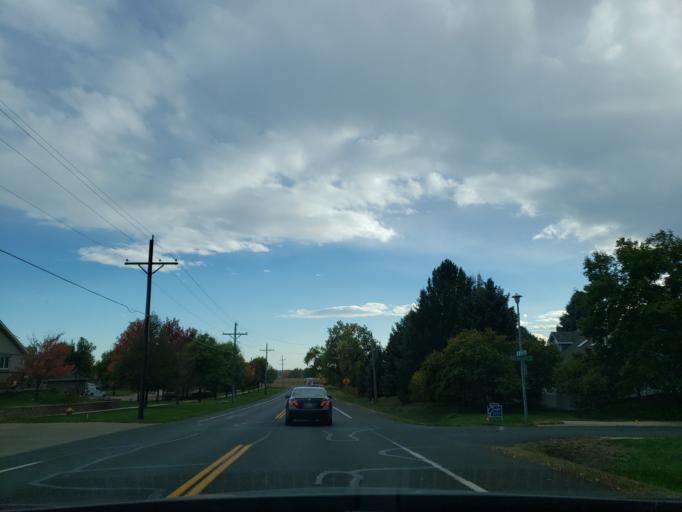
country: US
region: Colorado
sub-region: Larimer County
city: Fort Collins
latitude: 40.6122
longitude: -105.0386
